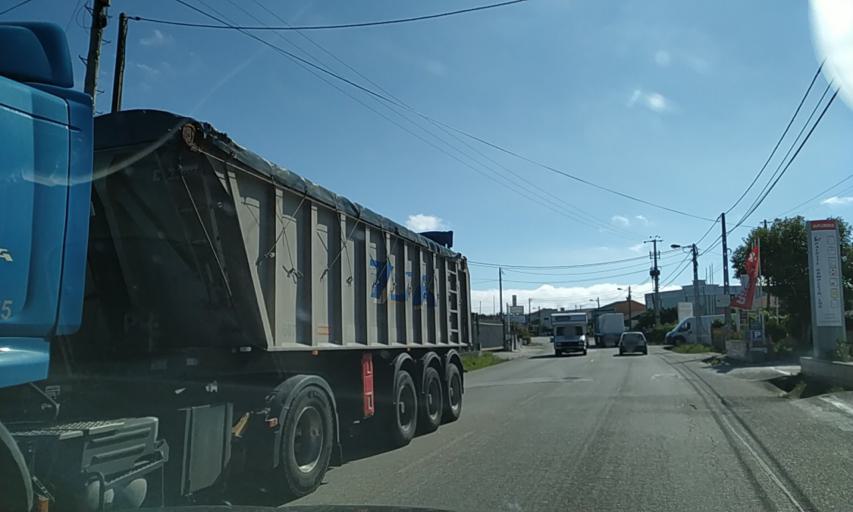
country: PT
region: Aveiro
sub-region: Aveiro
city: Aveiro
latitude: 40.6754
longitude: -8.6017
